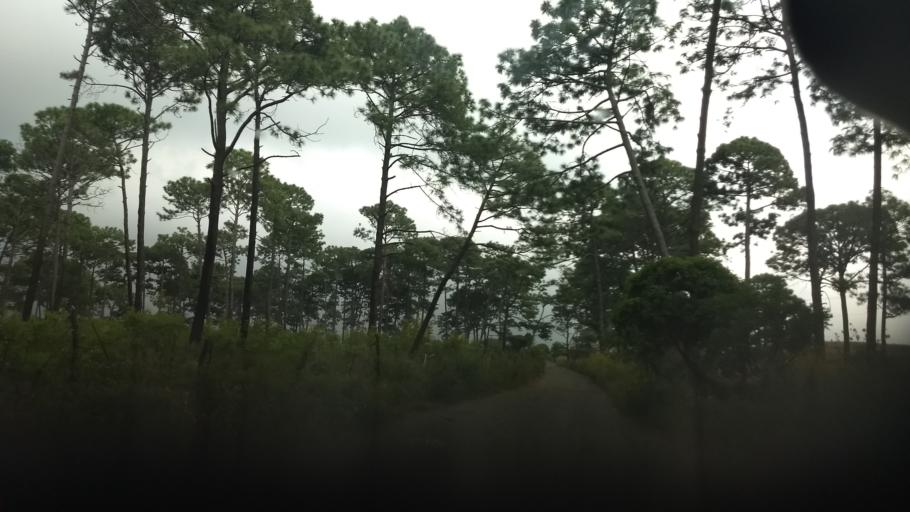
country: MX
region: Jalisco
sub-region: Tonila
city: San Marcos
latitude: 19.4627
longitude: -103.5267
